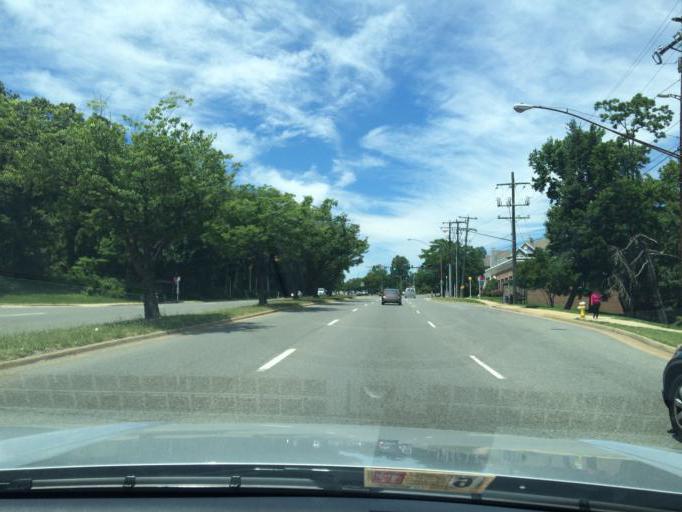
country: US
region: Virginia
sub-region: Fairfax County
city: Lincolnia
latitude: 38.8131
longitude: -77.1253
